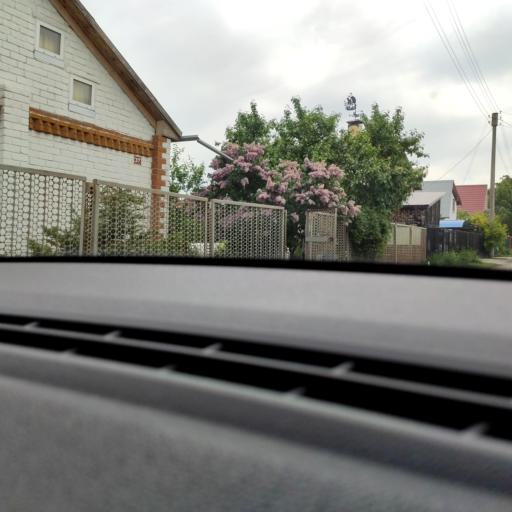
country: RU
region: Samara
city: Podstepki
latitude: 53.5040
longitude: 49.1609
